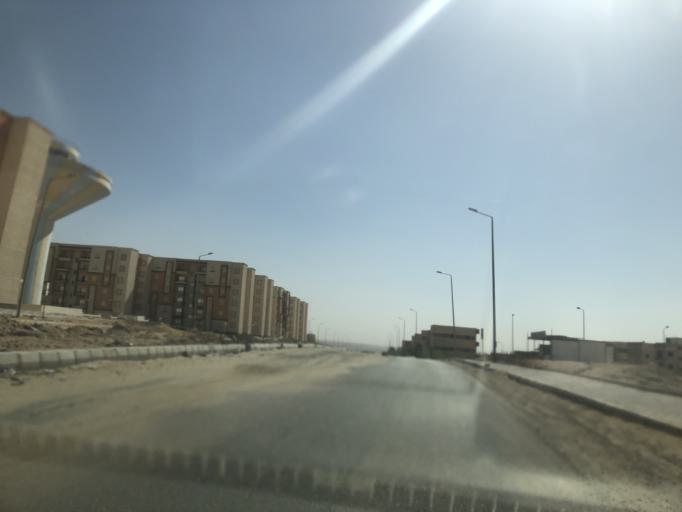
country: EG
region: Al Jizah
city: Madinat Sittah Uktubar
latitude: 29.9326
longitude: 30.9726
